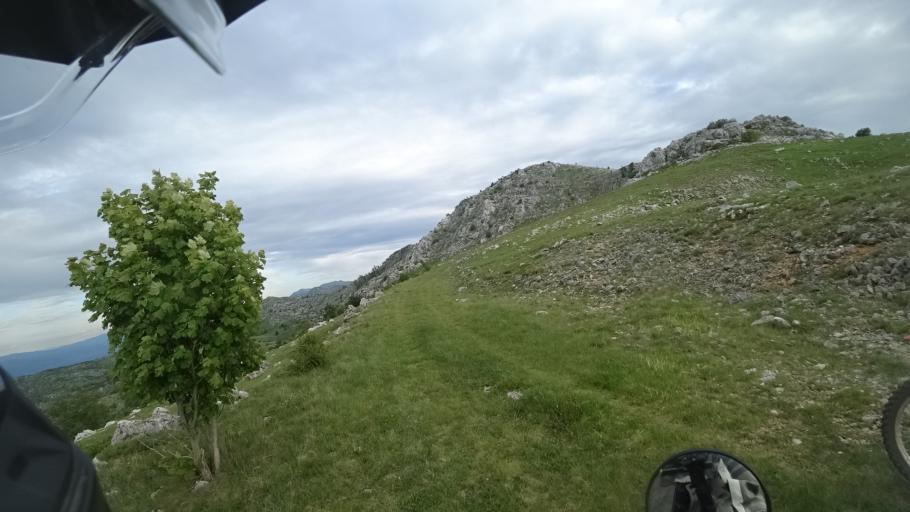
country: HR
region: Sibensko-Kniniska
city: Drnis
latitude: 43.8602
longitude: 16.3814
